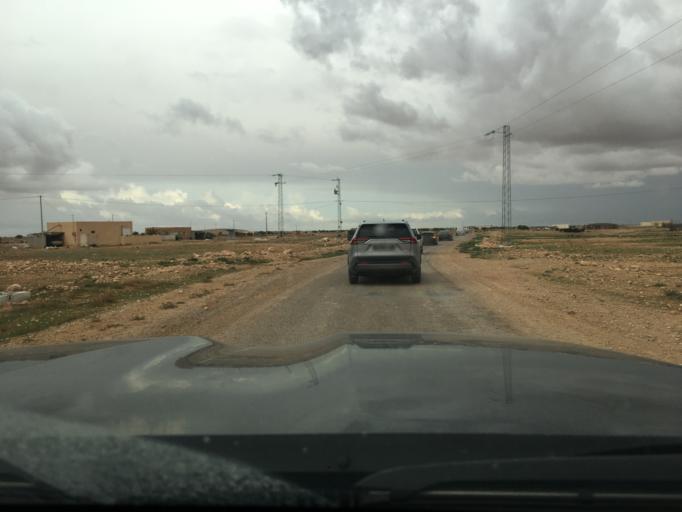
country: TN
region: Madanin
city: Medenine
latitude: 33.2919
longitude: 10.6070
